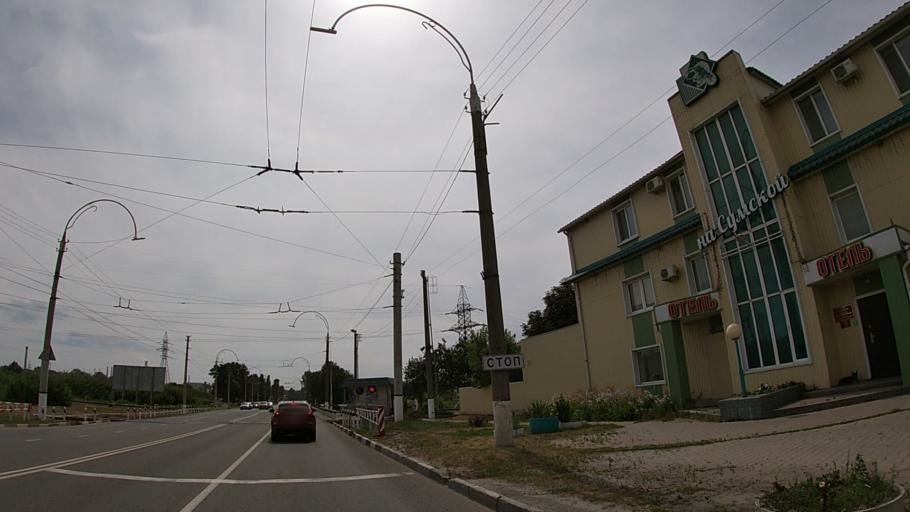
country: RU
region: Belgorod
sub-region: Belgorodskiy Rayon
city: Belgorod
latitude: 50.6124
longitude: 36.5371
